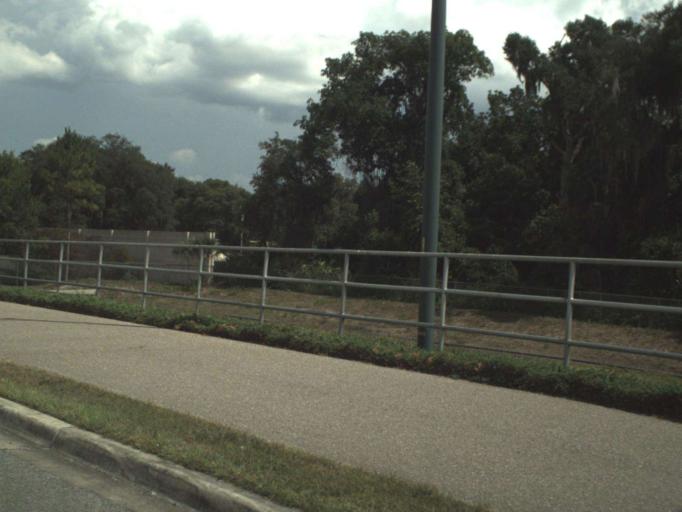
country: US
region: Florida
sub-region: Lake County
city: Silver Lake
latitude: 28.8200
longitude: -81.7781
